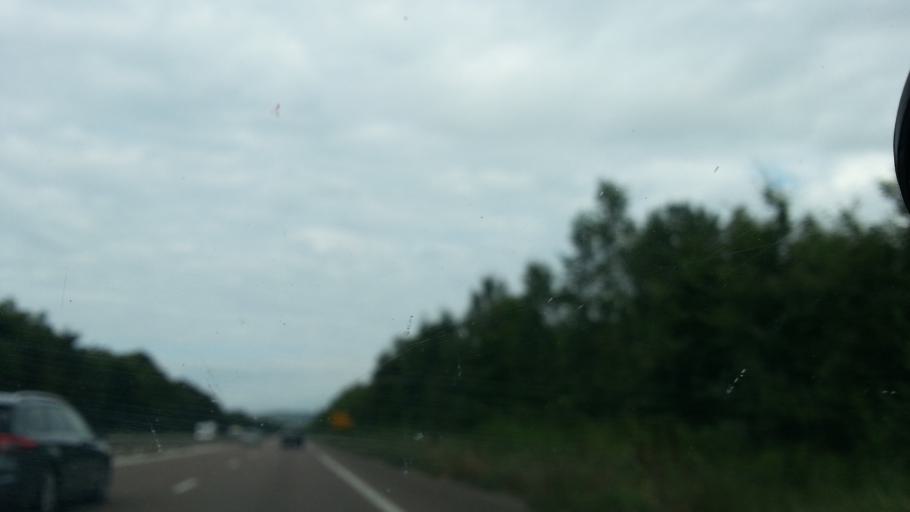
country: FR
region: Bourgogne
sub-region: Departement de Saone-et-Loire
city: Givry
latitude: 46.7582
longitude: 4.7716
